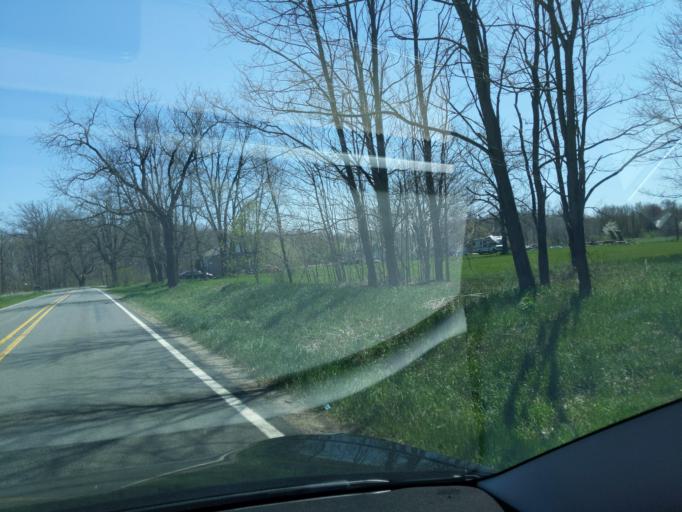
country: US
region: Michigan
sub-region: Ingham County
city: Stockbridge
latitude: 42.4975
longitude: -84.2287
